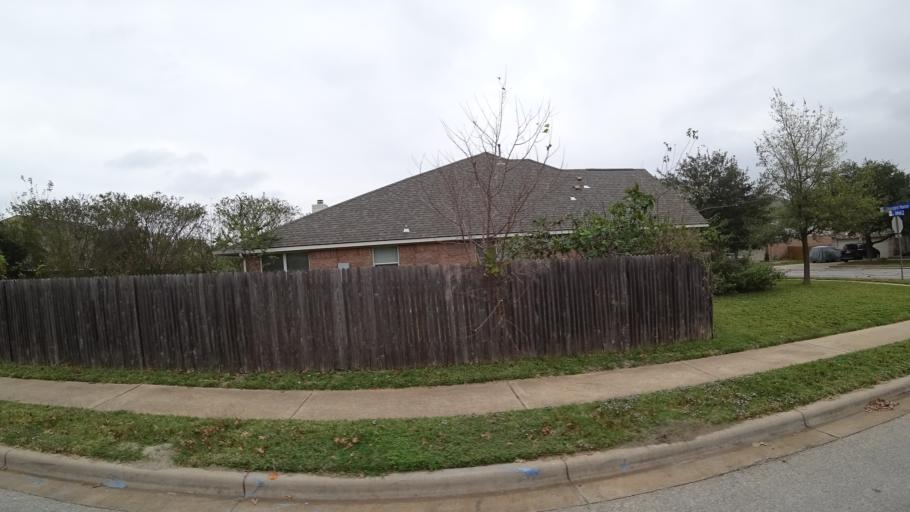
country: US
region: Texas
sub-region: Travis County
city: Pflugerville
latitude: 30.4301
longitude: -97.6166
